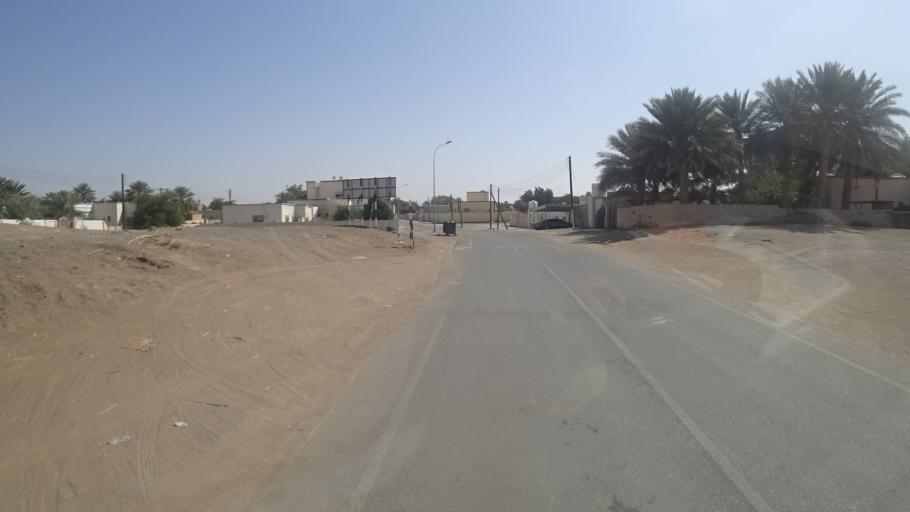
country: OM
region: Ash Sharqiyah
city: Badiyah
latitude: 22.4984
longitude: 58.7387
